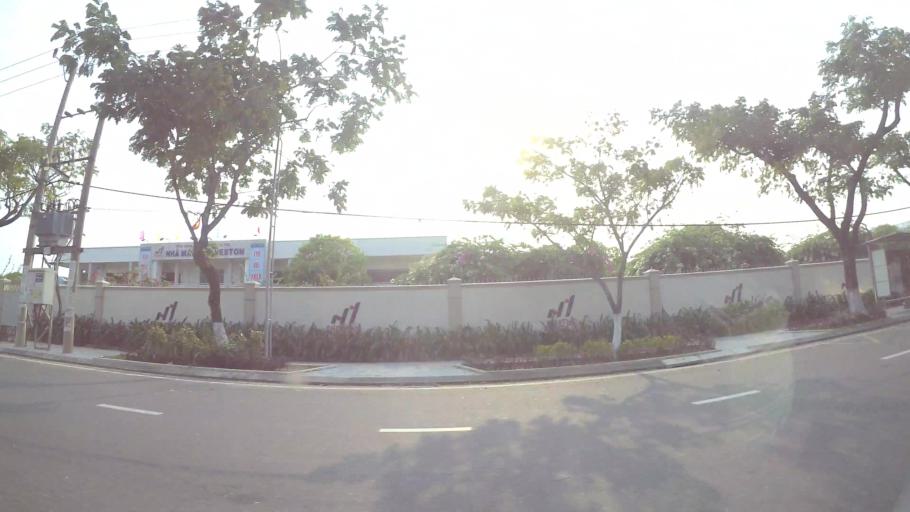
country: VN
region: Da Nang
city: Cam Le
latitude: 16.0199
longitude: 108.2033
